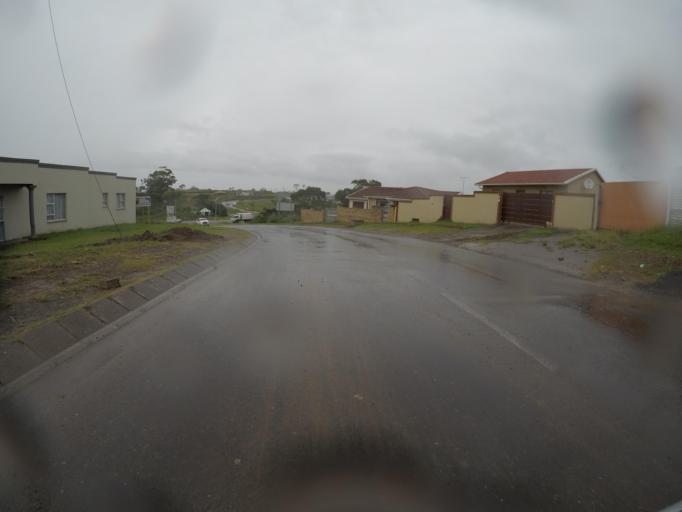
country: ZA
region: Eastern Cape
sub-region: Buffalo City Metropolitan Municipality
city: East London
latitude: -32.9988
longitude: 27.8422
